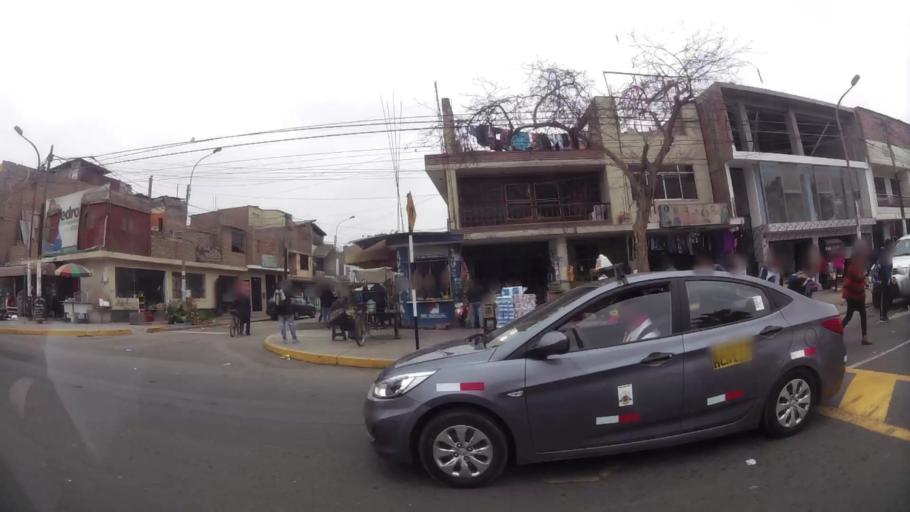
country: PE
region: Lima
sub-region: Lima
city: Independencia
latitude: -11.9358
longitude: -77.0755
